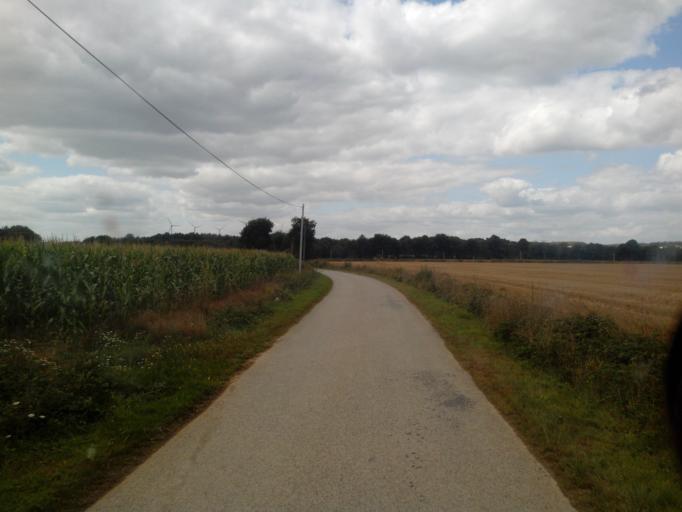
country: FR
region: Brittany
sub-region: Departement du Morbihan
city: Meneac
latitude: 48.1203
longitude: -2.4206
